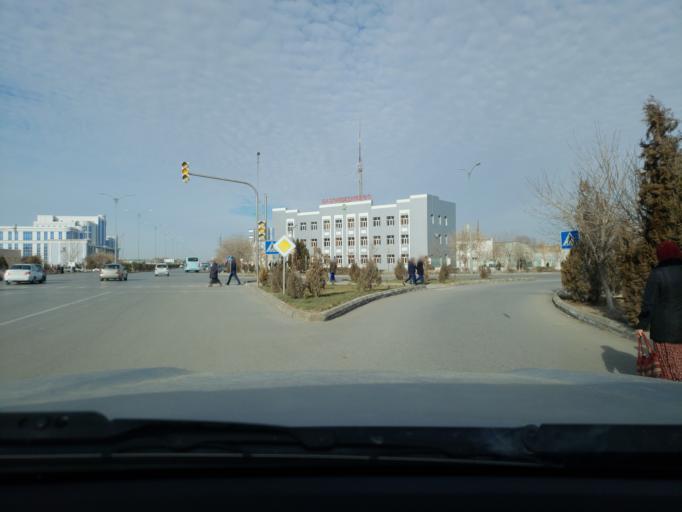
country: TM
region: Dasoguz
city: Dasoguz
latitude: 41.8458
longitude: 59.9637
